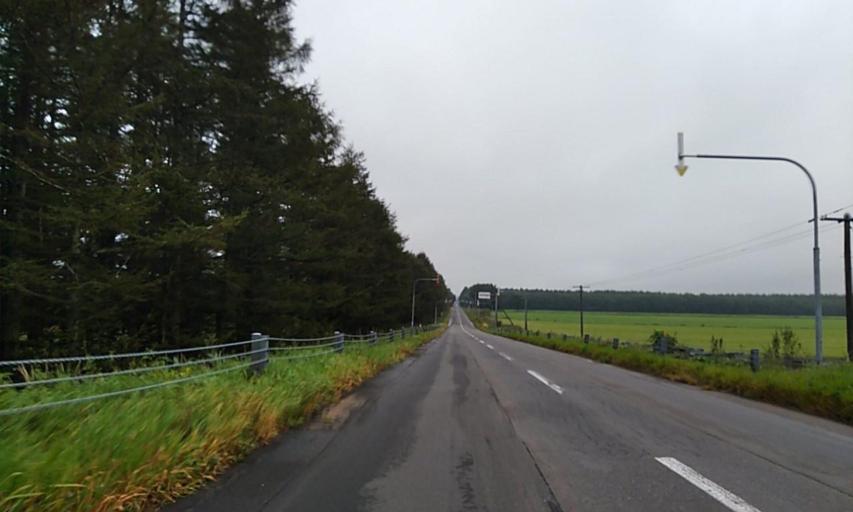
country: JP
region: Hokkaido
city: Shibetsu
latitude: 43.5057
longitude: 144.6628
